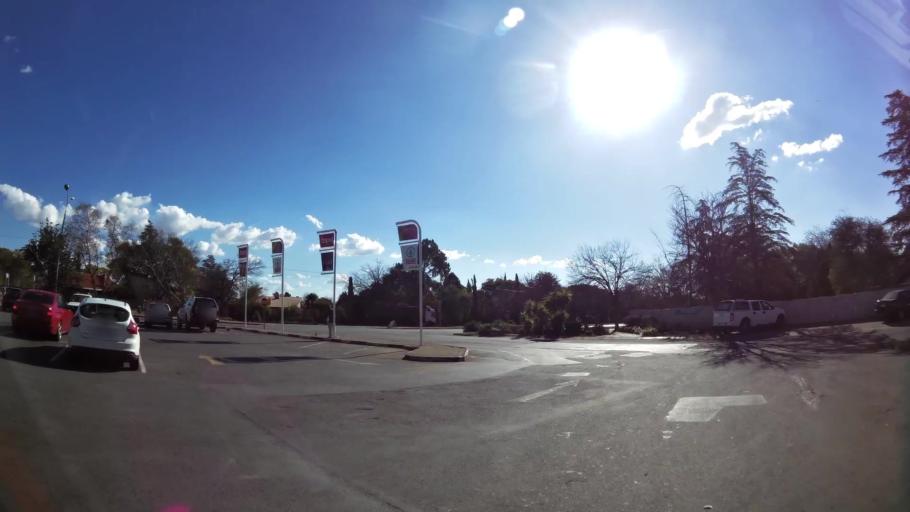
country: ZA
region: Gauteng
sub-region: West Rand District Municipality
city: Carletonville
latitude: -26.3727
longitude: 27.4064
